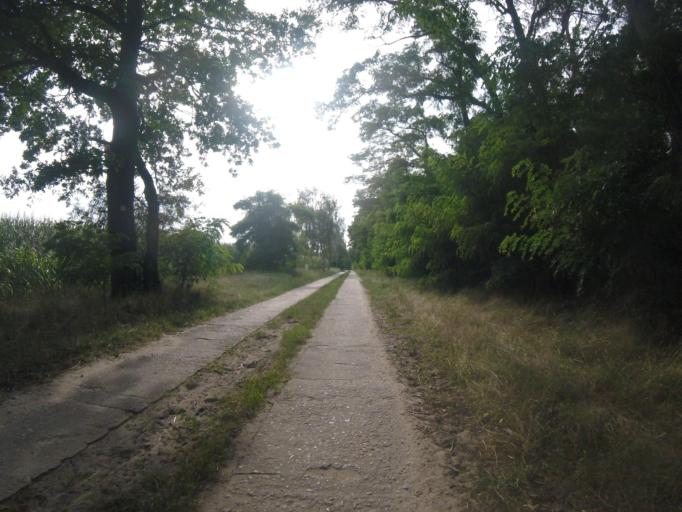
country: DE
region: Brandenburg
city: Rangsdorf
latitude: 52.2775
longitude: 13.4792
